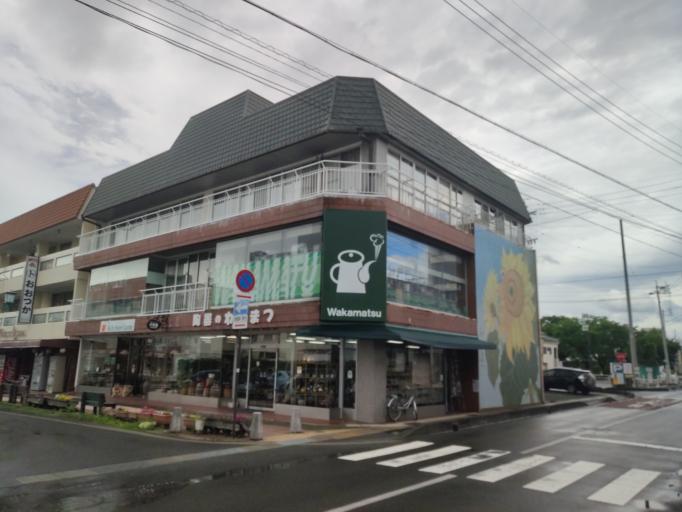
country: JP
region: Nagano
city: Saku
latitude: 36.2298
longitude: 138.4777
